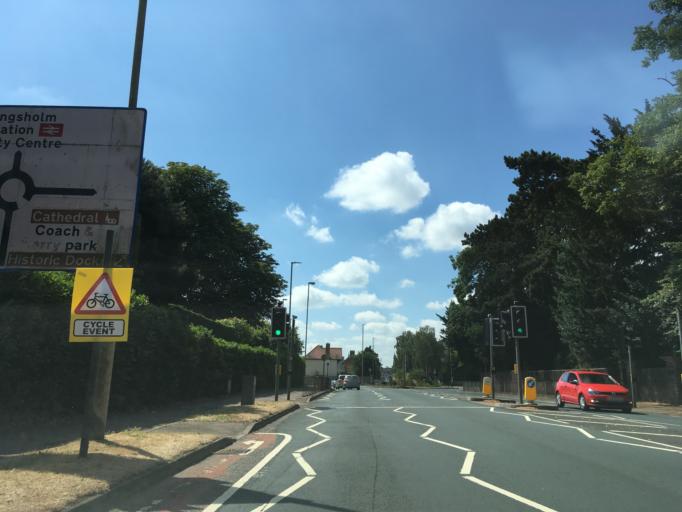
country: GB
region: England
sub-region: Gloucestershire
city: Gloucester
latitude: 51.8768
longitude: -2.2405
